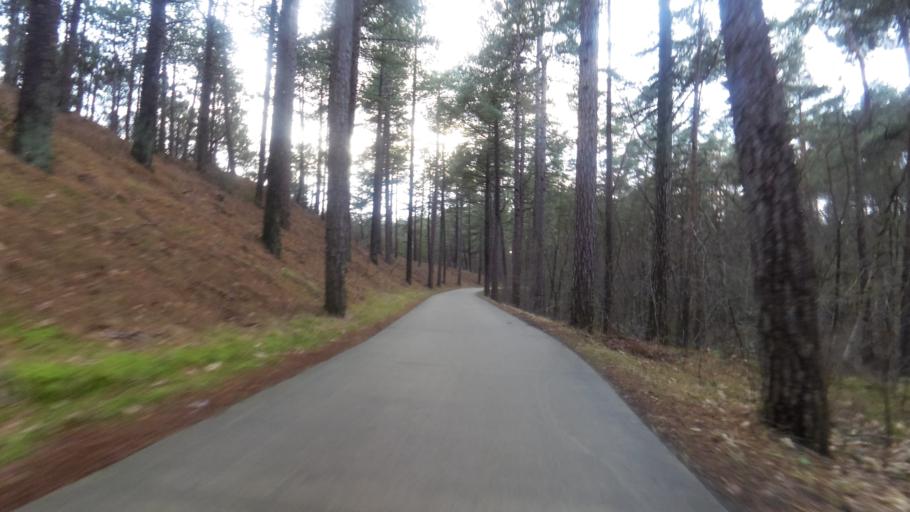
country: NL
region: North Holland
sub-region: Gemeente Heiloo
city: Heiloo
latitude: 52.6849
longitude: 4.6792
